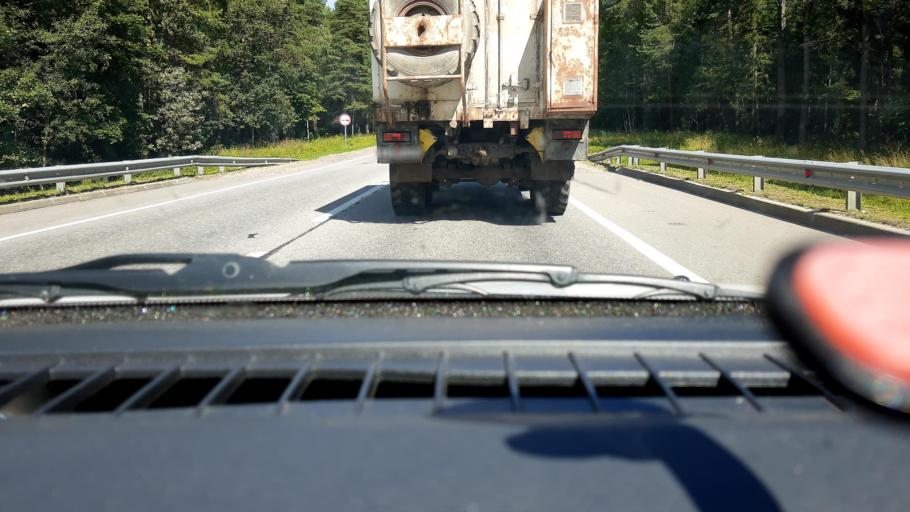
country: RU
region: Nizjnij Novgorod
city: Surovatikha
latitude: 55.7263
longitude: 43.9890
